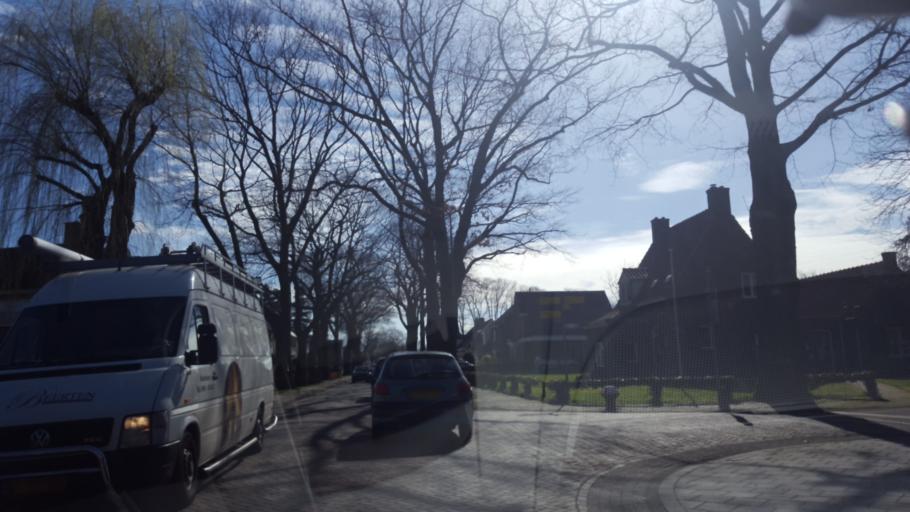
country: NL
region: North Brabant
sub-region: Gemeente Cranendonck
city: Cranendonck
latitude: 51.3502
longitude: 5.6126
